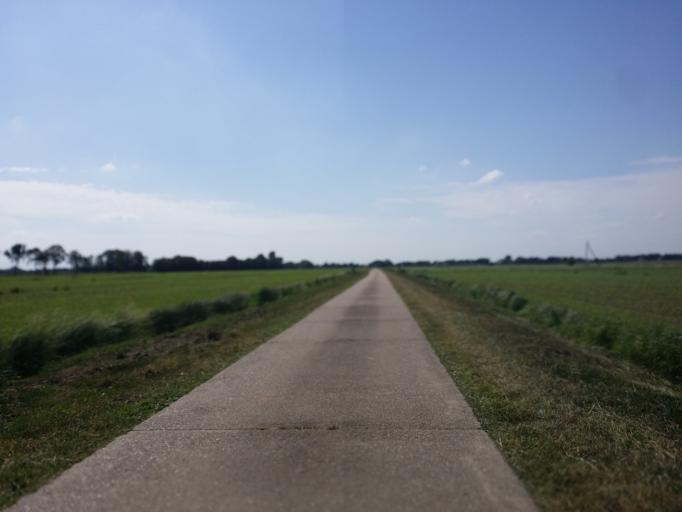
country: DE
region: Lower Saxony
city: Elsfleth
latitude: 53.2013
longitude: 8.4219
